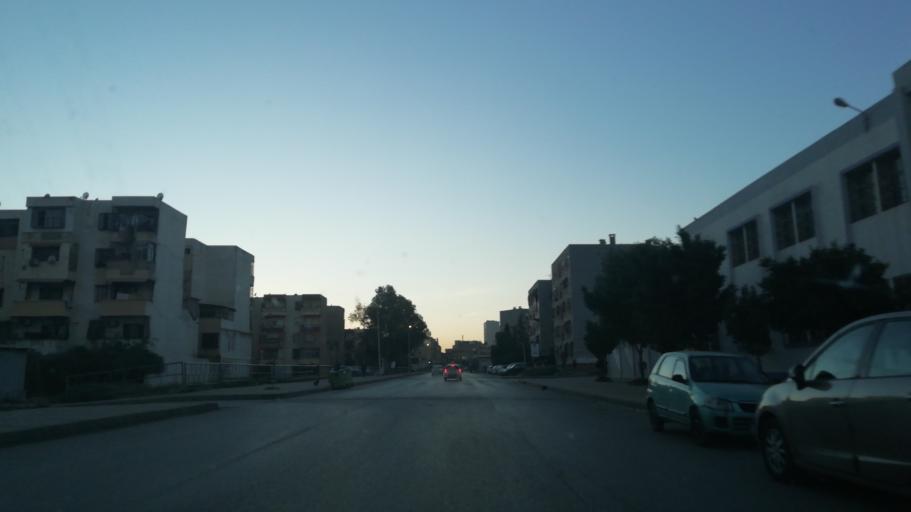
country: DZ
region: Oran
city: Oran
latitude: 35.6984
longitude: -0.5920
